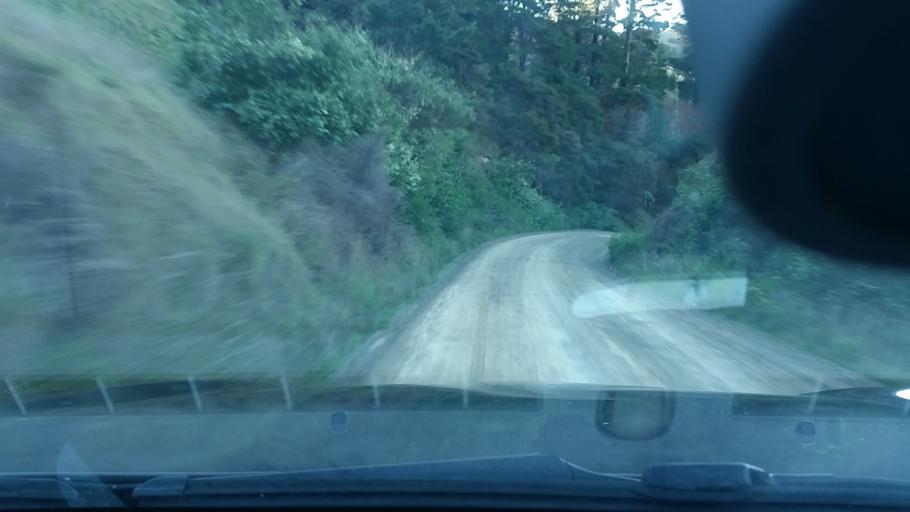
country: NZ
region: Marlborough
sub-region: Marlborough District
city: Blenheim
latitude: -41.5802
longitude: 174.0631
